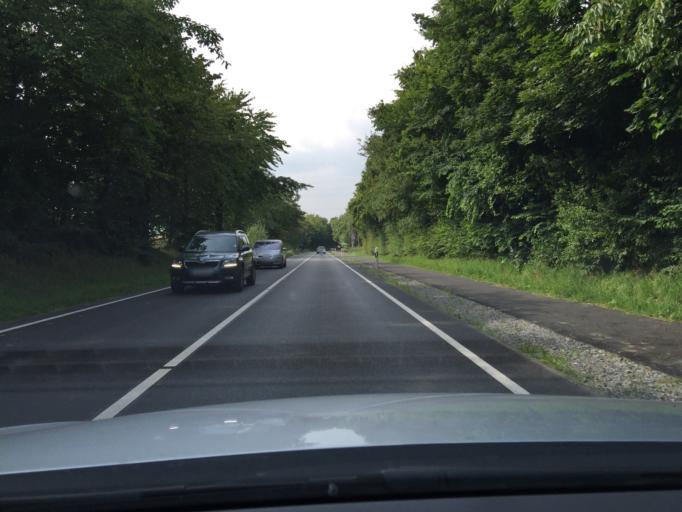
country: DE
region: North Rhine-Westphalia
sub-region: Regierungsbezirk Dusseldorf
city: Velbert
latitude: 51.3538
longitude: 7.0859
